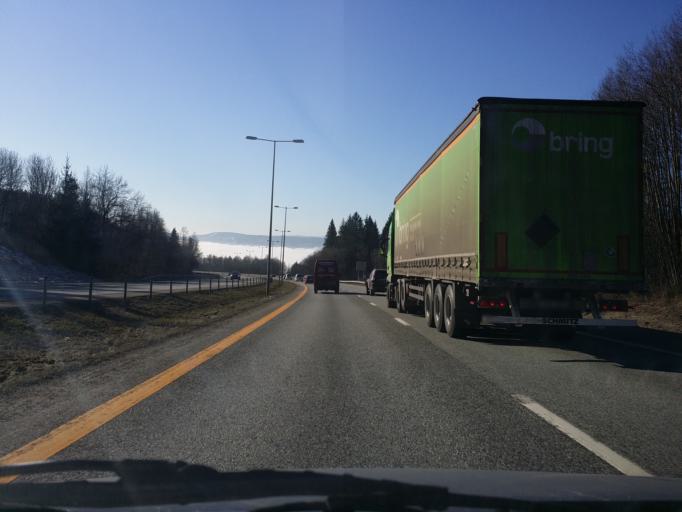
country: NO
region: Buskerud
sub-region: Lier
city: Tranby
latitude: 59.8021
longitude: 10.2695
